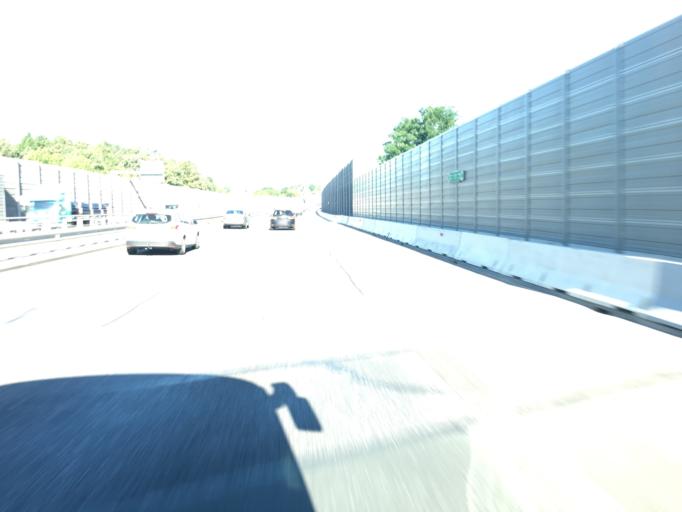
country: SI
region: Celje
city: Celje
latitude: 46.2538
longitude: 15.2609
